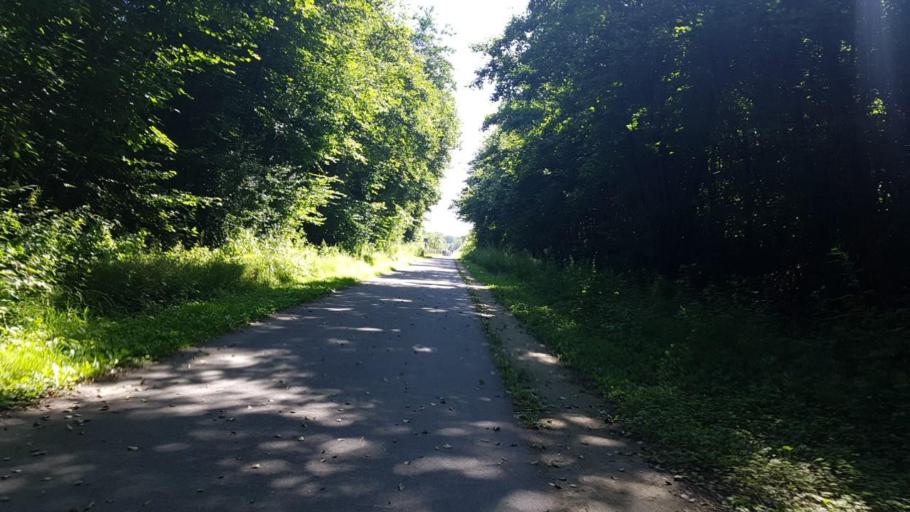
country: BE
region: Wallonia
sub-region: Province du Hainaut
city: Momignies
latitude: 50.0270
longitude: 4.1781
